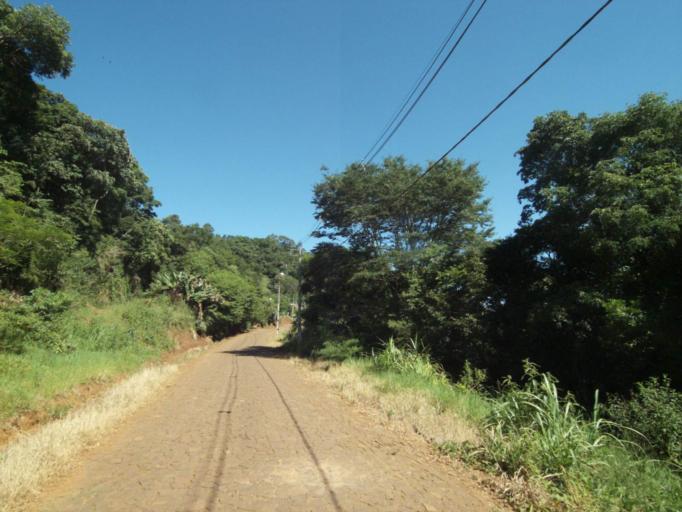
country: BR
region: Parana
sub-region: Ampere
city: Ampere
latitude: -26.1667
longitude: -53.3614
